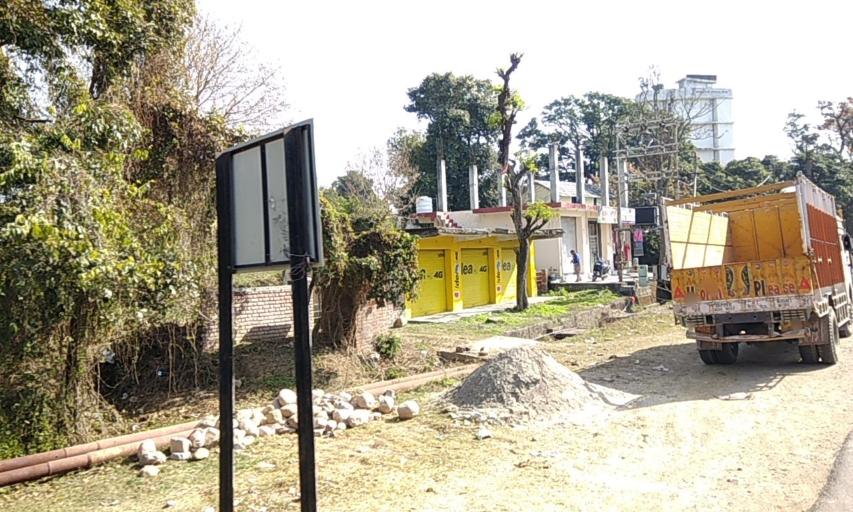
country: IN
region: Himachal Pradesh
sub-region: Kangra
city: Yol
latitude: 32.2207
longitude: 76.1756
